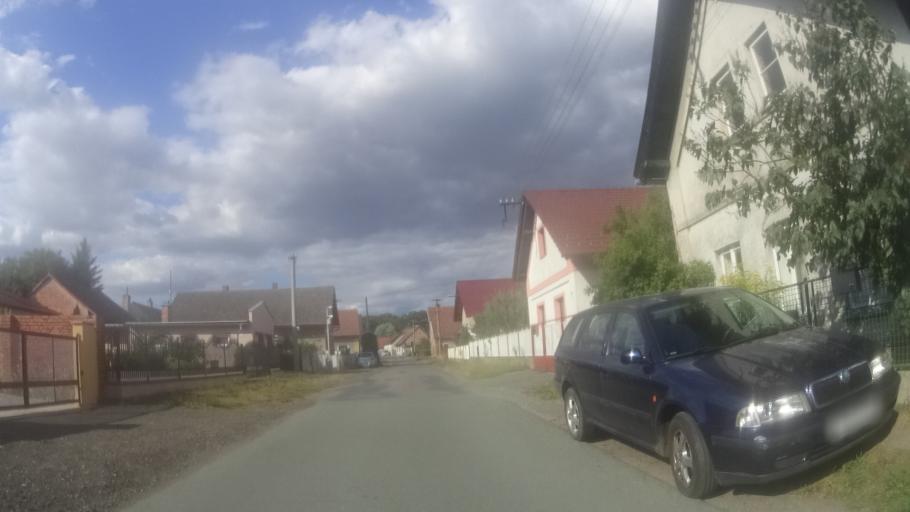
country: CZ
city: Albrechtice nad Orlici
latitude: 50.1710
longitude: 16.0318
